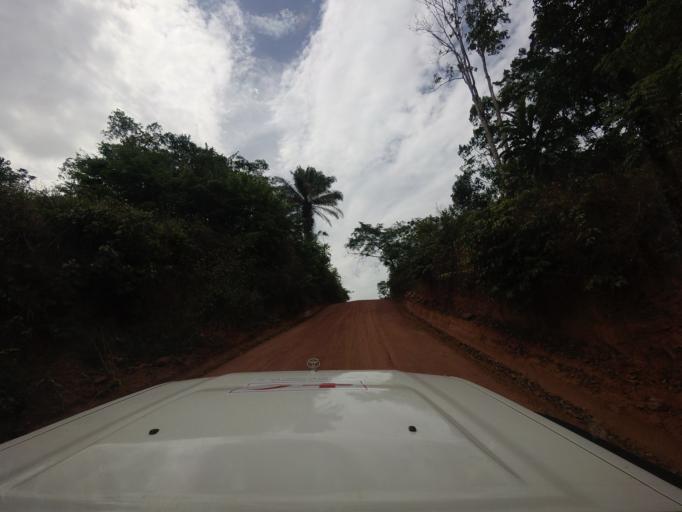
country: SL
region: Eastern Province
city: Buedu
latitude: 8.2284
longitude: -10.2236
